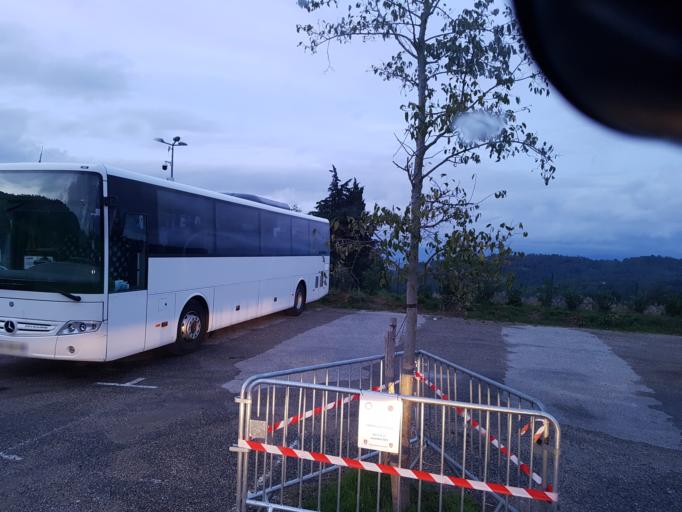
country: FR
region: Provence-Alpes-Cote d'Azur
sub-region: Departement du Var
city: La Garde-Freinet
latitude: 43.3193
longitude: 6.4700
